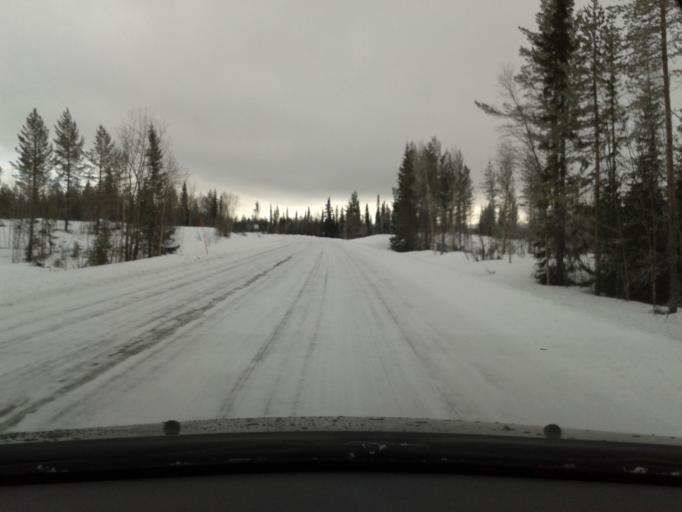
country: SE
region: Vaesterbotten
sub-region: Vilhelmina Kommun
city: Sjoberg
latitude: 64.8106
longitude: 15.9763
